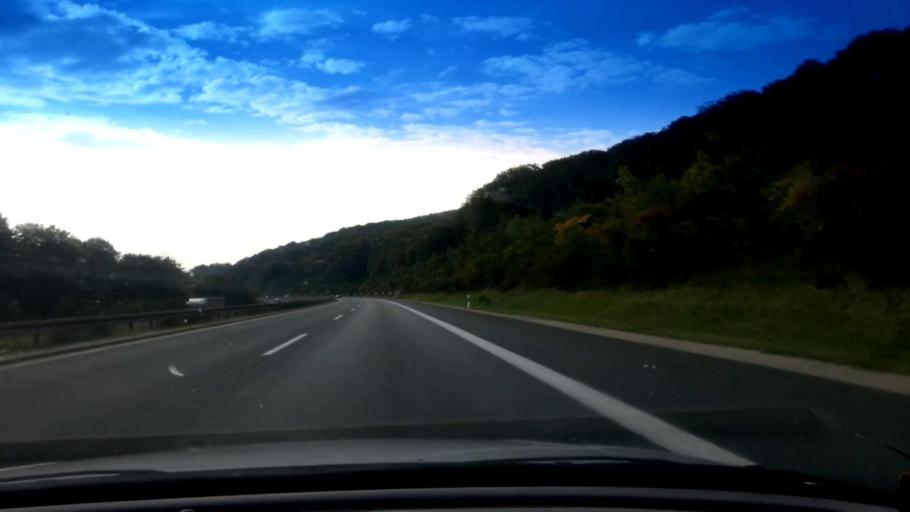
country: DE
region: Bavaria
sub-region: Upper Franconia
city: Schesslitz
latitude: 49.9840
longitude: 11.0822
